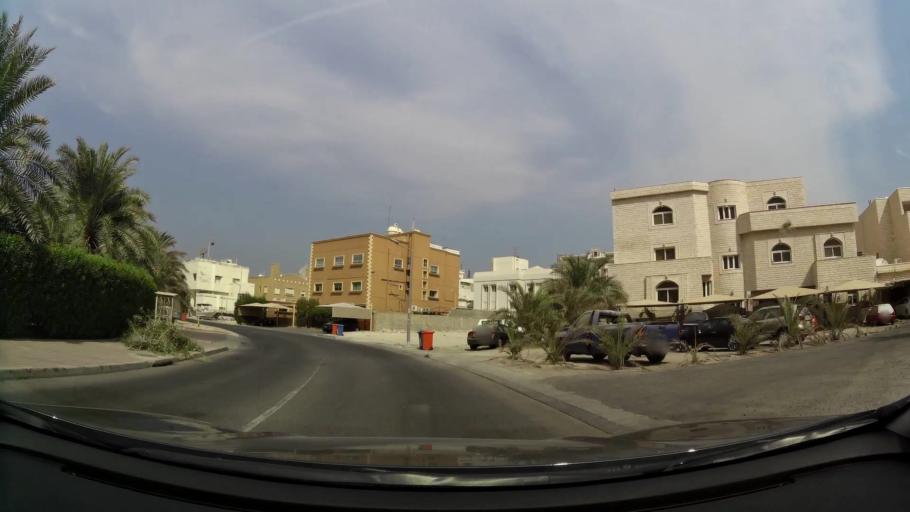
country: KW
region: Al Asimah
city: Ad Dasmah
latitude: 29.3511
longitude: 47.9908
